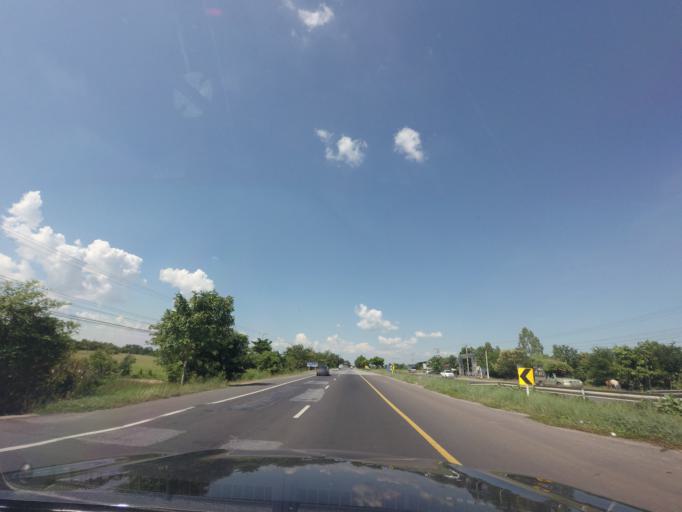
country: TH
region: Nakhon Ratchasima
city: Non Sung
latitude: 15.2000
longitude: 102.3516
